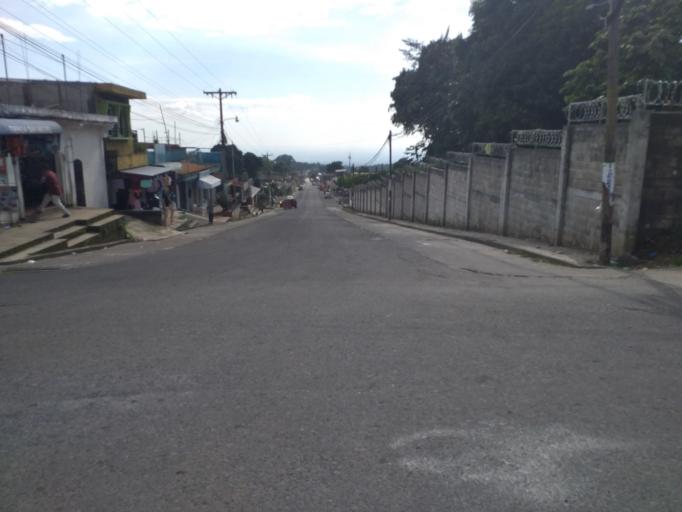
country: GT
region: Suchitepeque
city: Pueblo Nuevo
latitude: 14.6471
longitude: -91.5548
